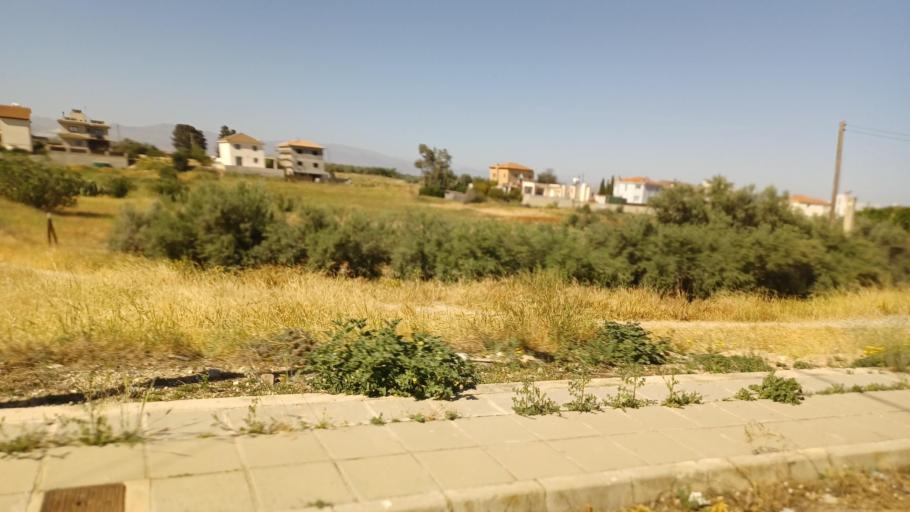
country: CY
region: Lefkosia
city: Kokkinotrimithia
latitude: 35.1551
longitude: 33.1856
